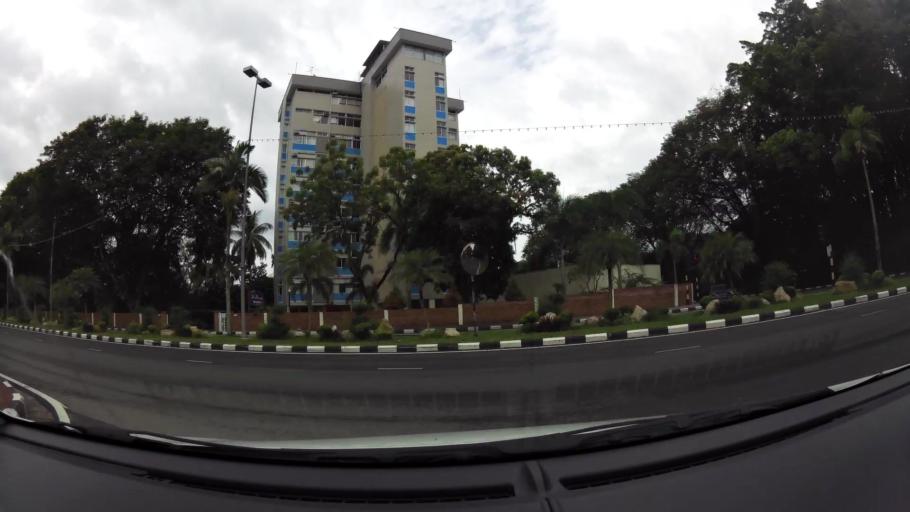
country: BN
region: Brunei and Muara
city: Bandar Seri Begawan
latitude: 4.8950
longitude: 114.9418
